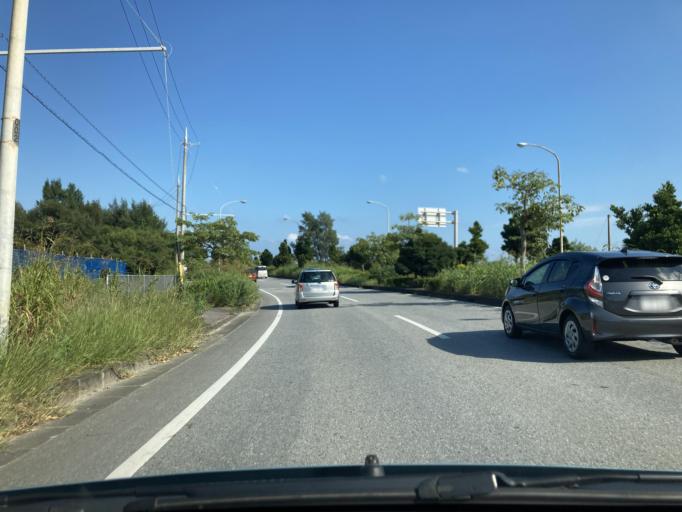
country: JP
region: Okinawa
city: Okinawa
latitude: 26.3015
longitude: 127.8119
